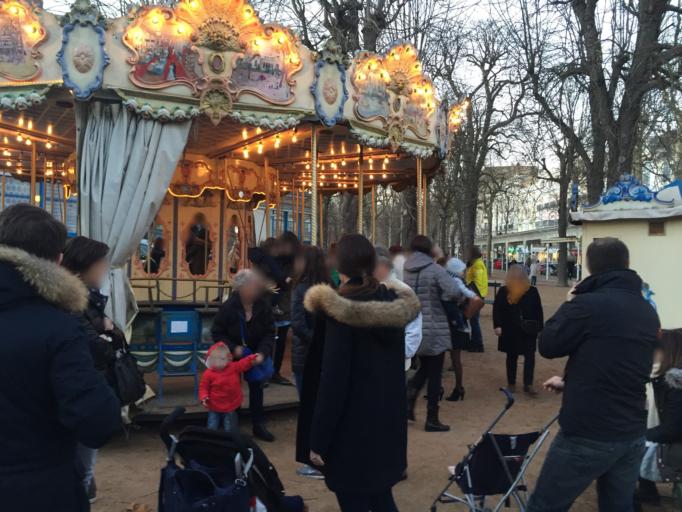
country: FR
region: Auvergne
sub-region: Departement de l'Allier
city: Vichy
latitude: 46.1231
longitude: 3.4219
